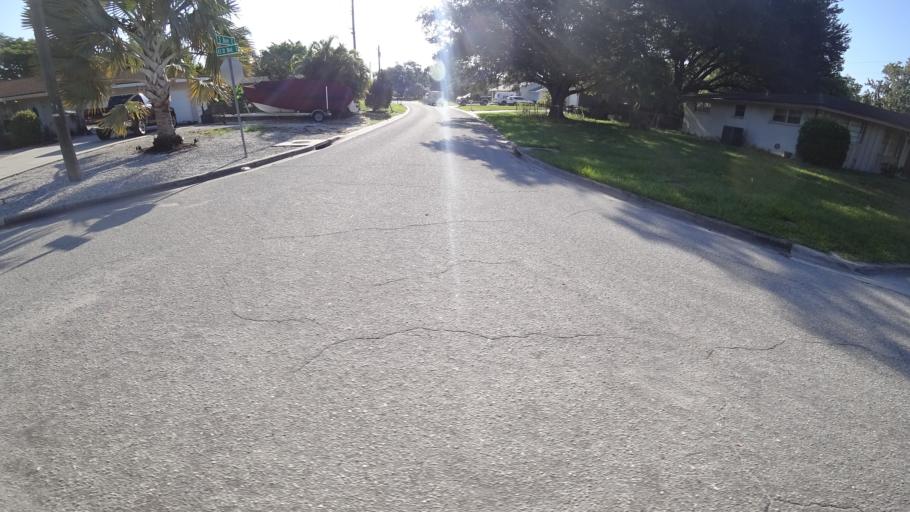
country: US
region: Florida
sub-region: Manatee County
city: Ellenton
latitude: 27.5004
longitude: -82.5088
